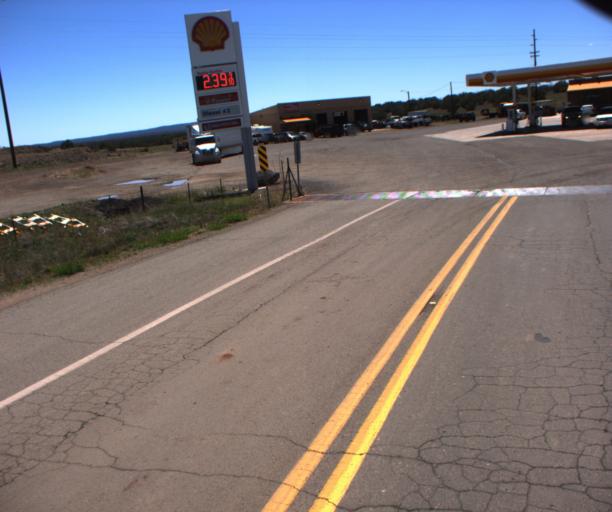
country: US
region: Arizona
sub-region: Coconino County
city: Williams
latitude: 35.2189
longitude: -112.4980
